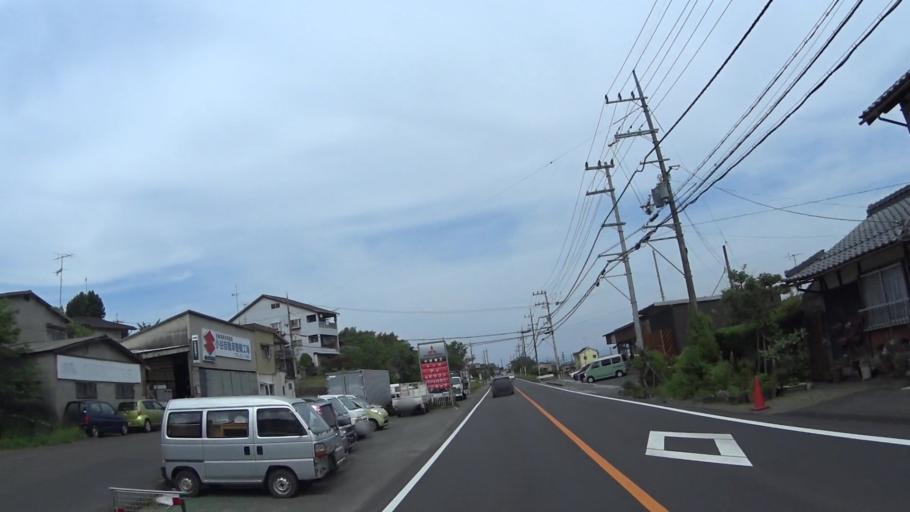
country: JP
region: Shiga Prefecture
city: Kitahama
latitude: 35.1331
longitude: 135.8938
